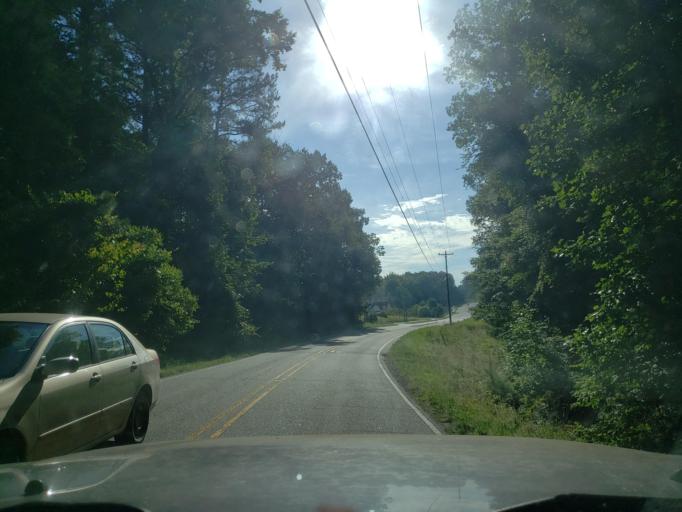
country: US
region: North Carolina
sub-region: Durham County
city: Durham
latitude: 35.9436
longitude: -78.8734
